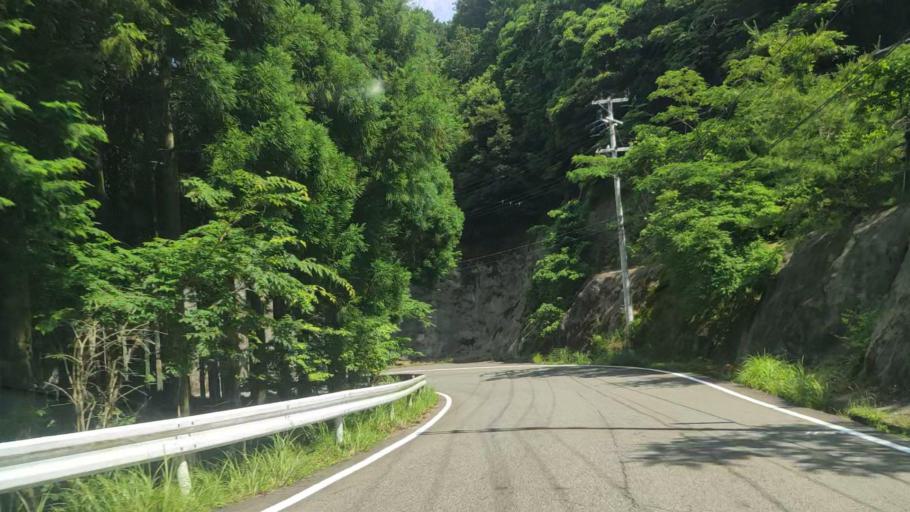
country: JP
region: Hyogo
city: Toyooka
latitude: 35.6401
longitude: 134.7666
